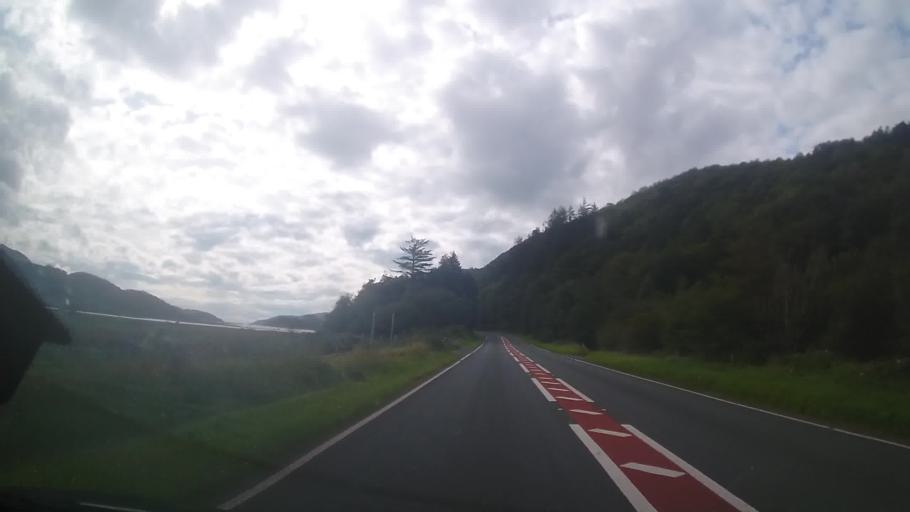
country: GB
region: Wales
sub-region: Gwynedd
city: Dolgellau
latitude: 52.7534
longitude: -3.9436
